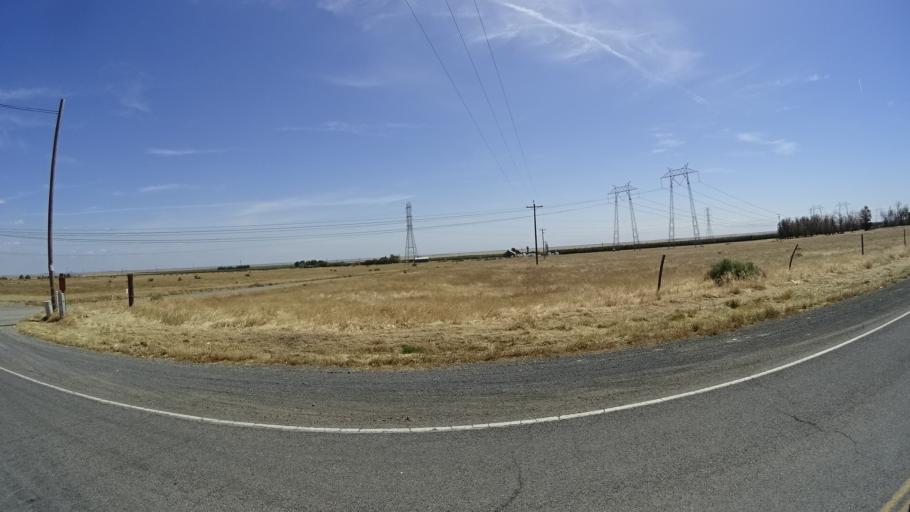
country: US
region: California
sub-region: Kings County
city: Kettleman City
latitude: 35.9928
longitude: -119.9561
